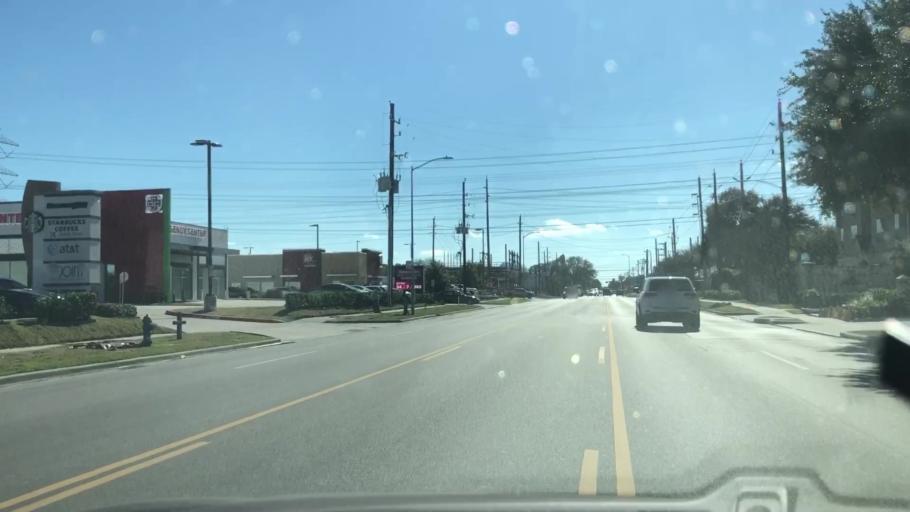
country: US
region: Texas
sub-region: Harris County
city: Bellaire
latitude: 29.7234
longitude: -95.4682
